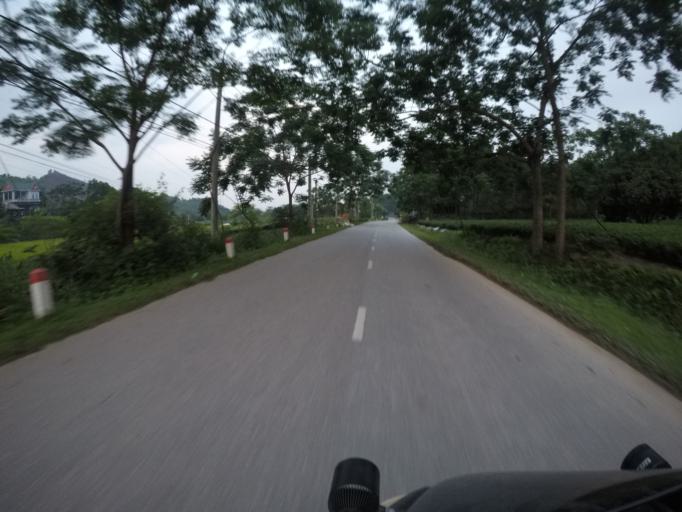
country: VN
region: Thai Nguyen
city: Chua Hang
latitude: 21.5881
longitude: 105.7319
